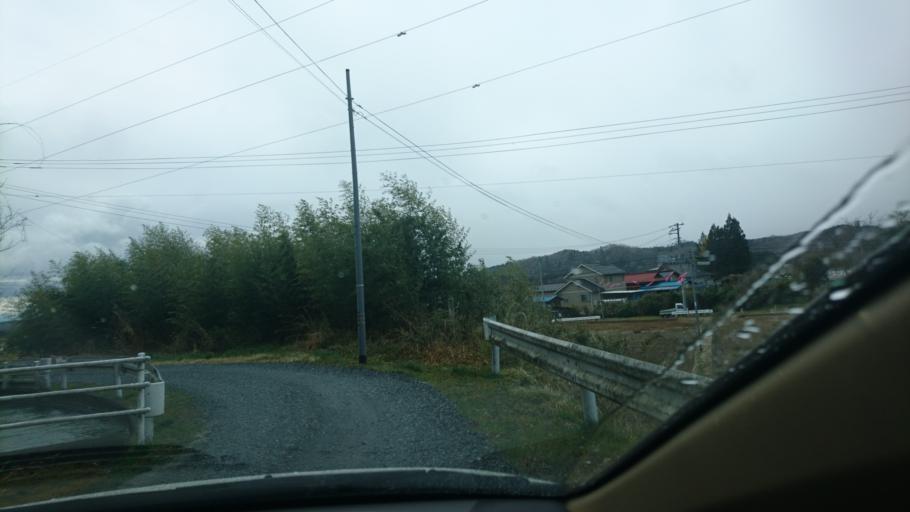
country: JP
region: Iwate
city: Ichinoseki
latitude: 38.9435
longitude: 141.0816
